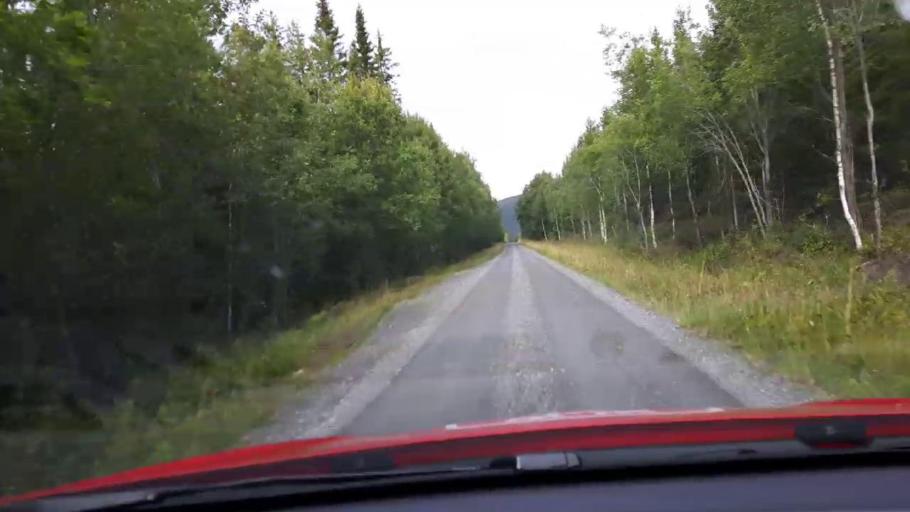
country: SE
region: Jaemtland
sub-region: Are Kommun
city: Are
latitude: 63.8059
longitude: 13.1124
